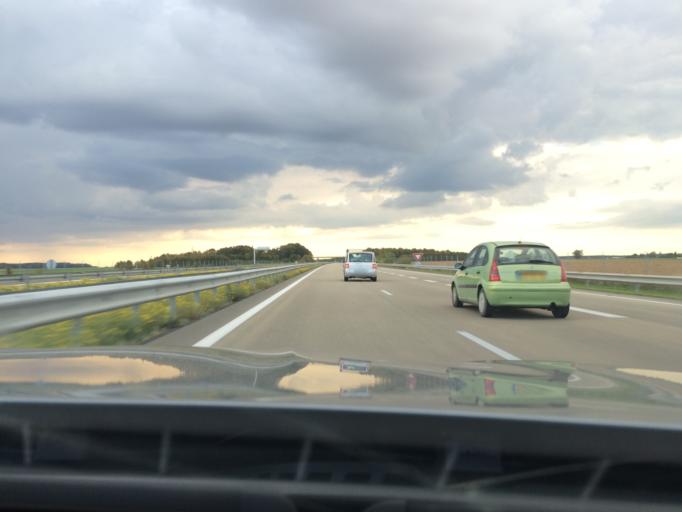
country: FR
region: Ile-de-France
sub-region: Departement de Seine-et-Marne
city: Egreville
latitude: 48.1876
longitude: 2.8244
